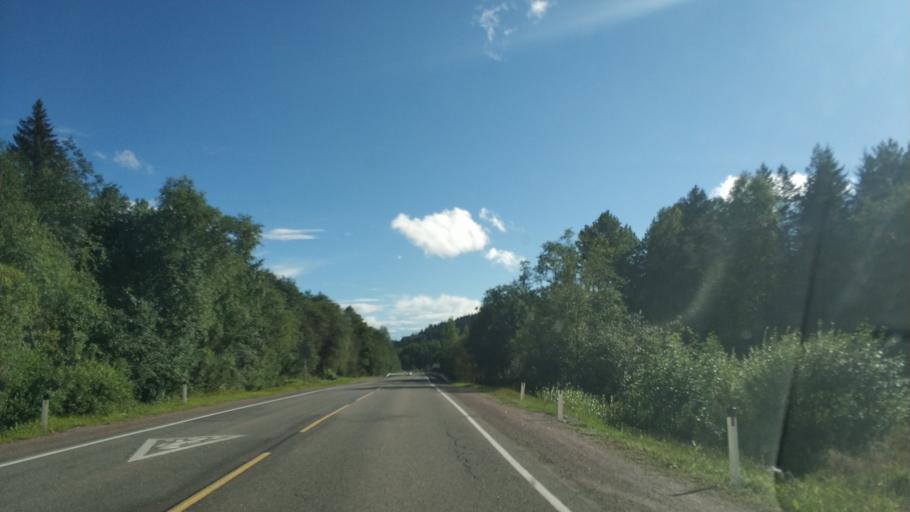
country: RU
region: Republic of Karelia
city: Sortavala
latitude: 61.6713
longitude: 30.6541
